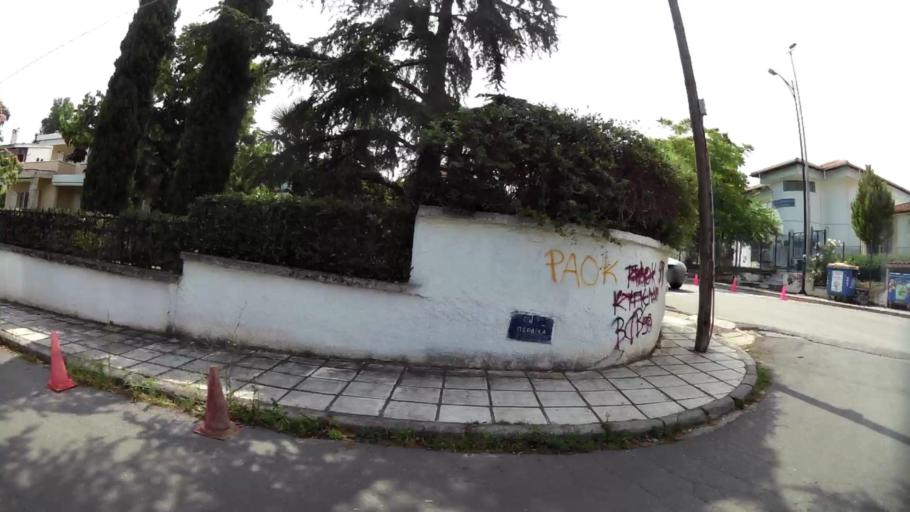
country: GR
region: Central Macedonia
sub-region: Nomos Thessalonikis
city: Panorama
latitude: 40.5818
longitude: 23.0157
